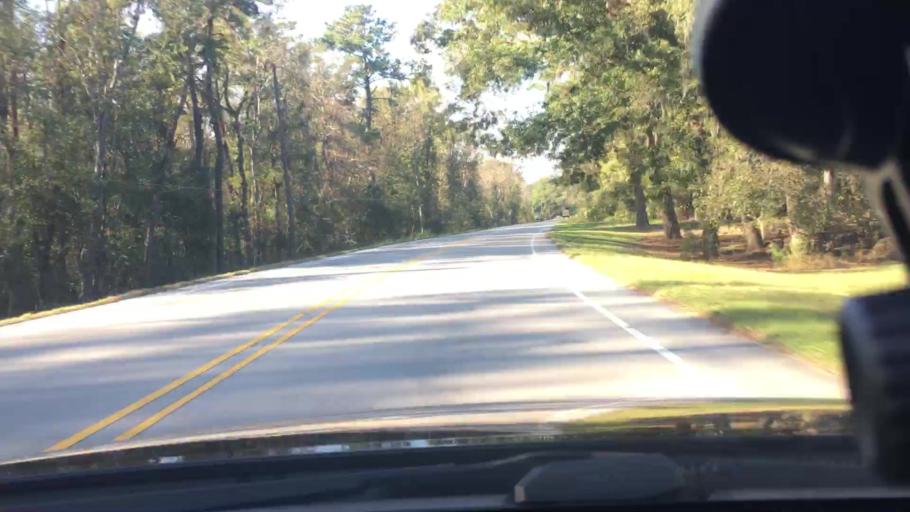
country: US
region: North Carolina
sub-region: Craven County
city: Vanceboro
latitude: 35.2298
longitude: -77.0722
